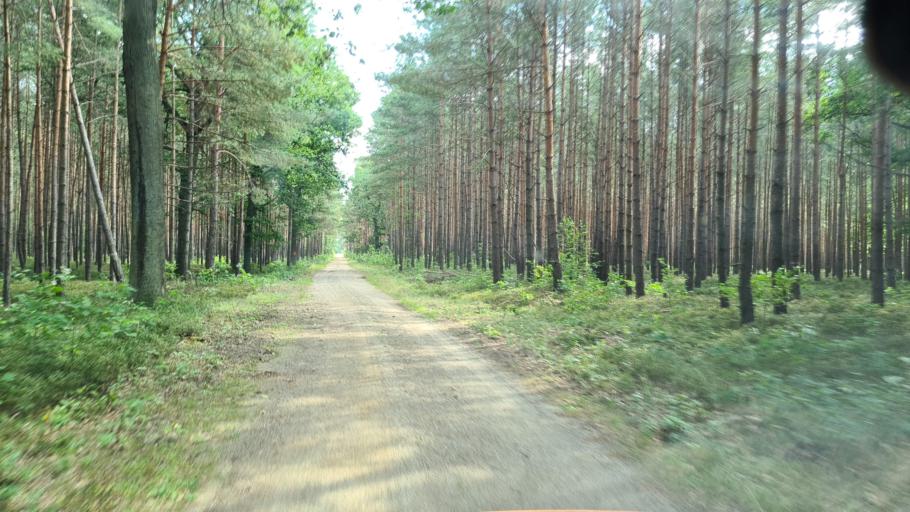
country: DE
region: Brandenburg
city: Hohenbucko
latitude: 51.7911
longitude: 13.5685
